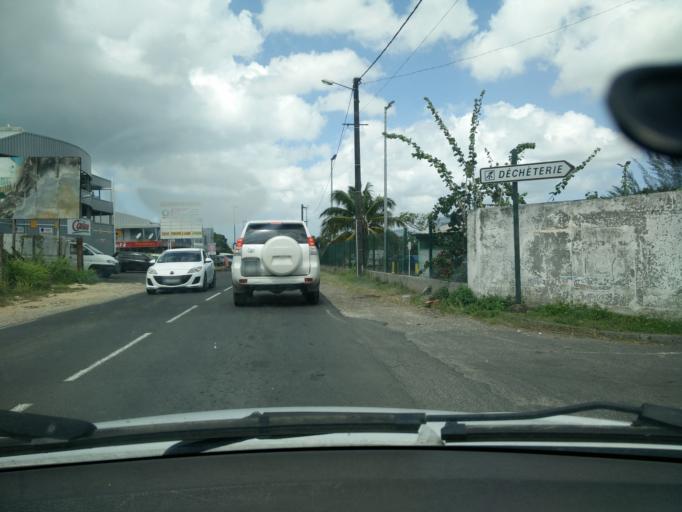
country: GP
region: Guadeloupe
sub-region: Guadeloupe
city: Les Abymes
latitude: 16.2594
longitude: -61.5098
